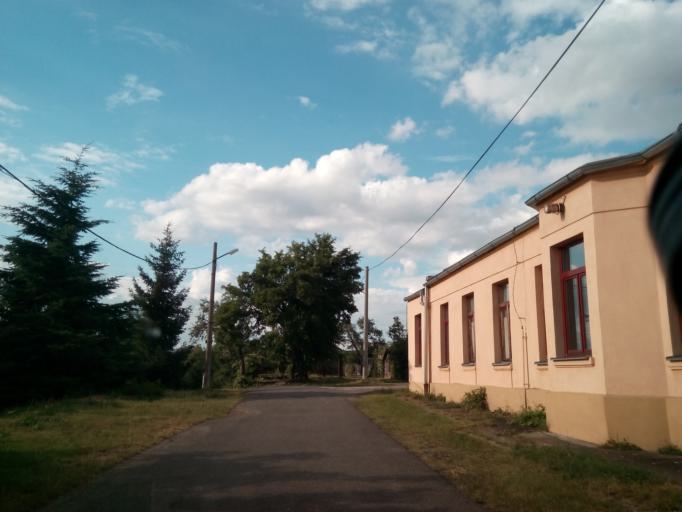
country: SK
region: Kosicky
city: Secovce
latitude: 48.5817
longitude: 21.5790
